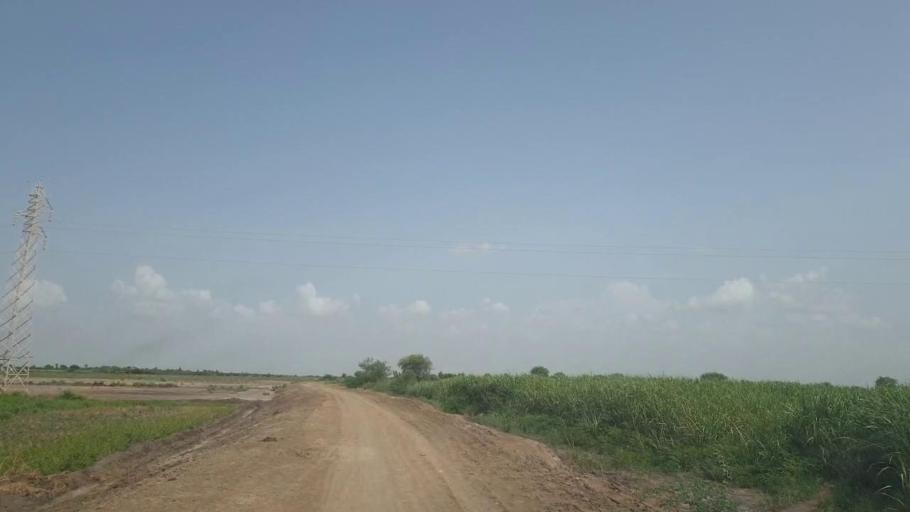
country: PK
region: Sindh
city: Tando Bago
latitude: 24.7562
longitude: 69.1705
